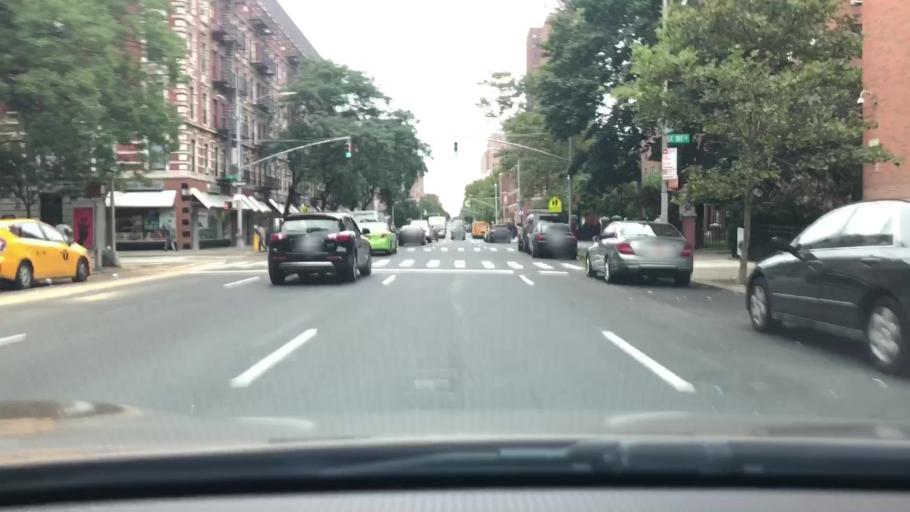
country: US
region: New York
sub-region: New York County
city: Manhattan
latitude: 40.7941
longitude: -73.9491
